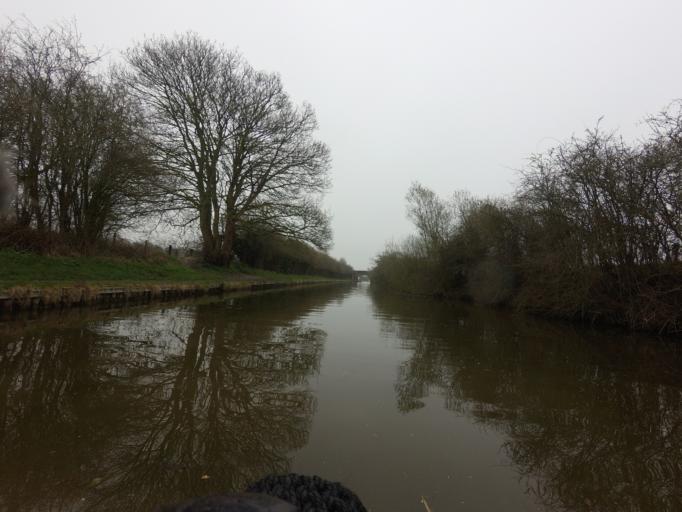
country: GB
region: England
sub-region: Hertfordshire
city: Tring
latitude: 51.7908
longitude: -0.6191
